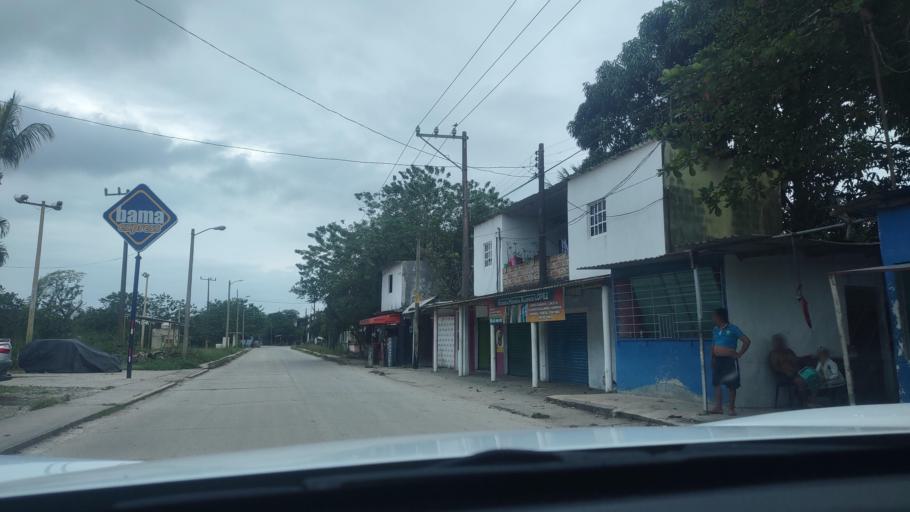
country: MX
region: Veracruz
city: Villa Nanchital
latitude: 18.0451
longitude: -94.3497
